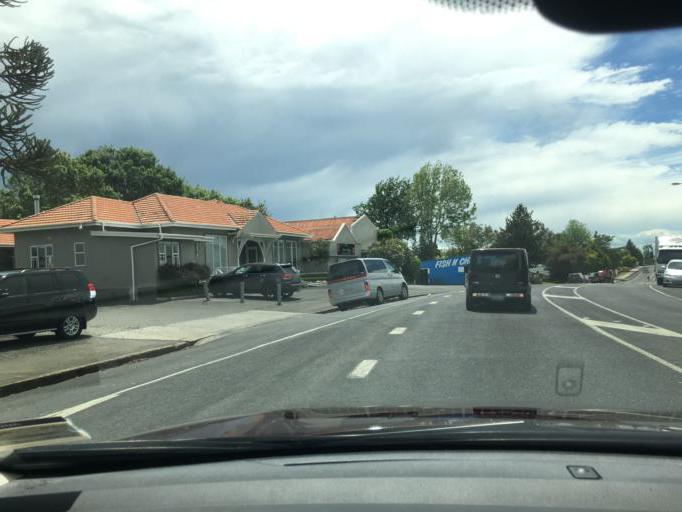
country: NZ
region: Waikato
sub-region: Hamilton City
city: Hamilton
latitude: -37.9190
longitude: 175.3069
